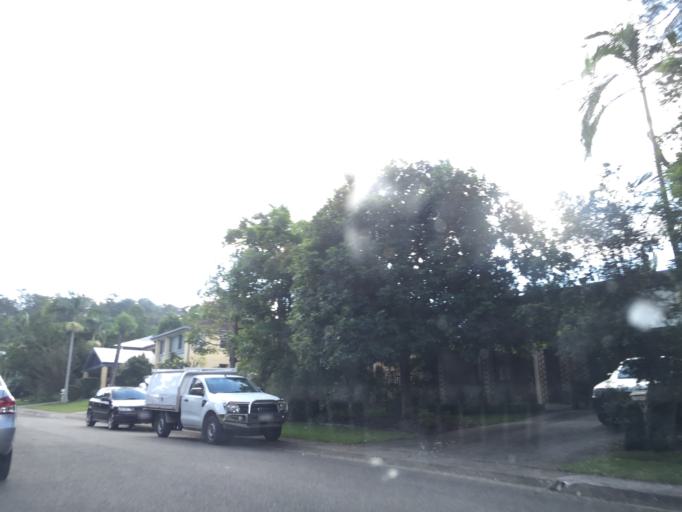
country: AU
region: Queensland
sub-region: Moreton Bay
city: Ferny Hills
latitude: -27.4374
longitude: 152.9306
